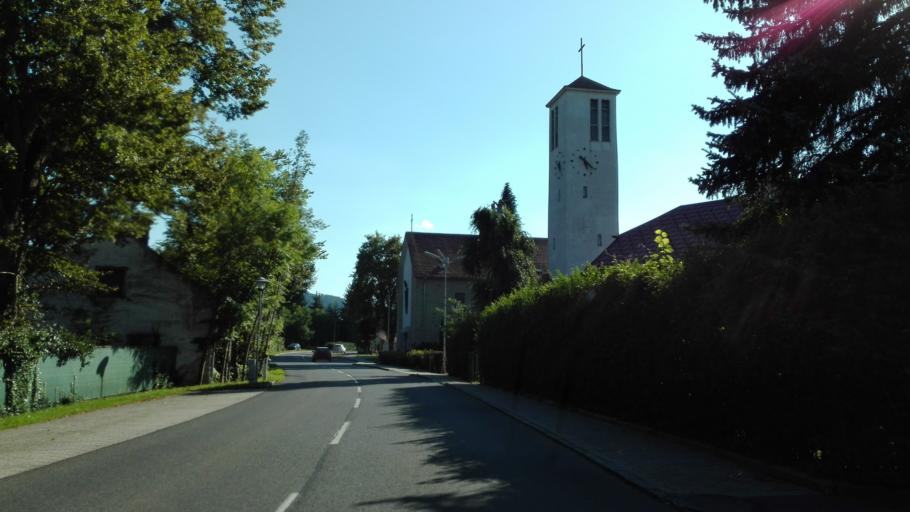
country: AT
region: Lower Austria
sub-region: Politischer Bezirk Sankt Polten
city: Altlengbach
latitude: 48.1328
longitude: 15.9130
